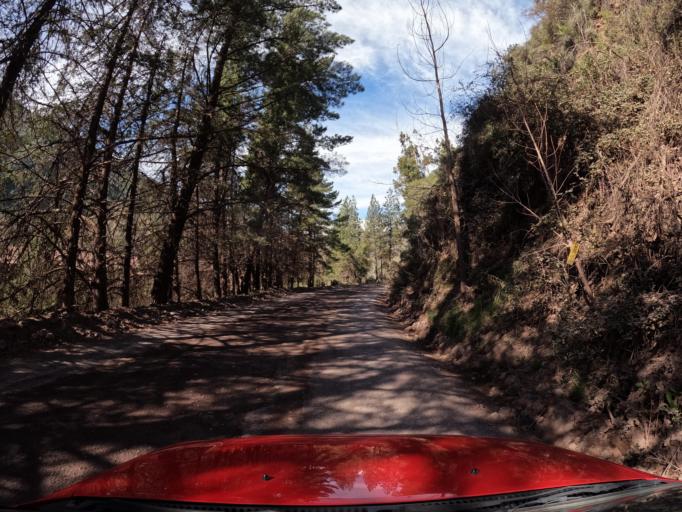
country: CL
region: O'Higgins
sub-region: Provincia de Colchagua
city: Chimbarongo
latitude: -35.0082
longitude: -70.7504
